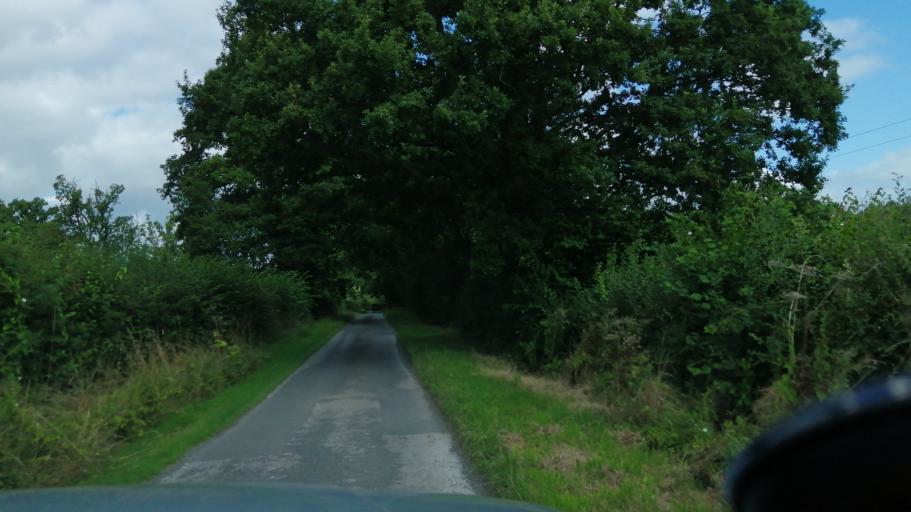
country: GB
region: England
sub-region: Herefordshire
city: Kinnersley
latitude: 52.1301
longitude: -2.9308
